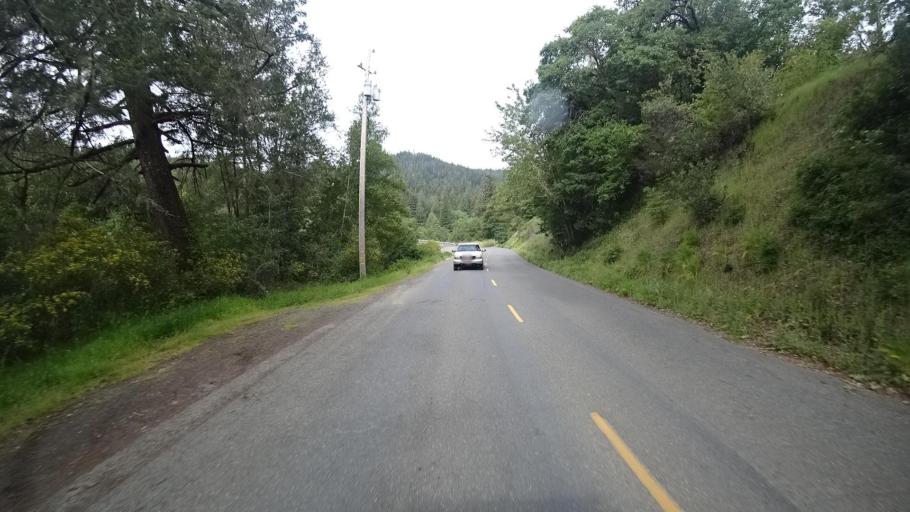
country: US
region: California
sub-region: Humboldt County
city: Redway
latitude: 40.2182
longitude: -123.8144
